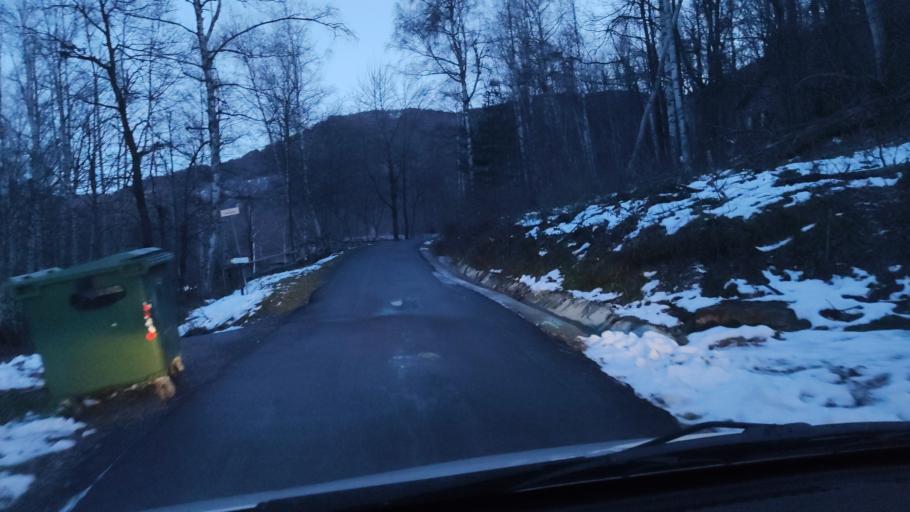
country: IT
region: Piedmont
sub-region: Provincia di Cuneo
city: Viola
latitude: 44.2750
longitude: 7.9680
